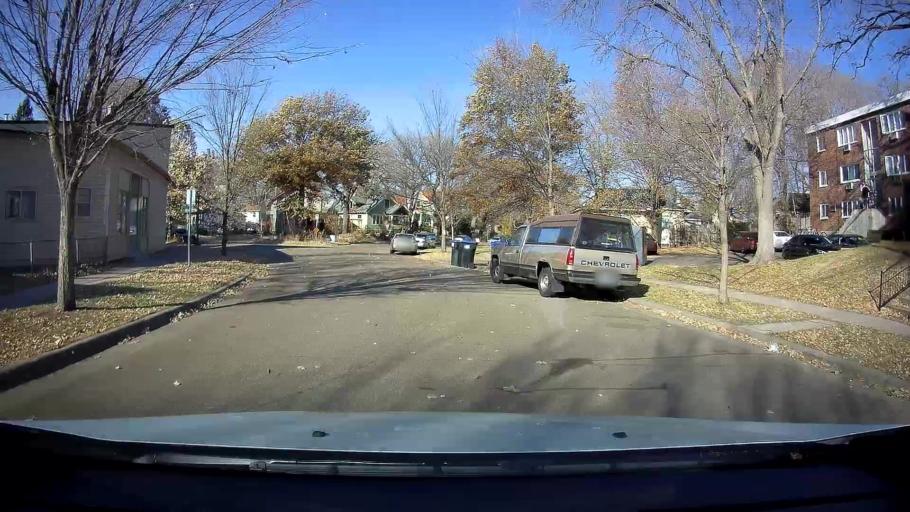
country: US
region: Minnesota
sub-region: Ramsey County
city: Falcon Heights
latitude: 44.9633
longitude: -93.1800
